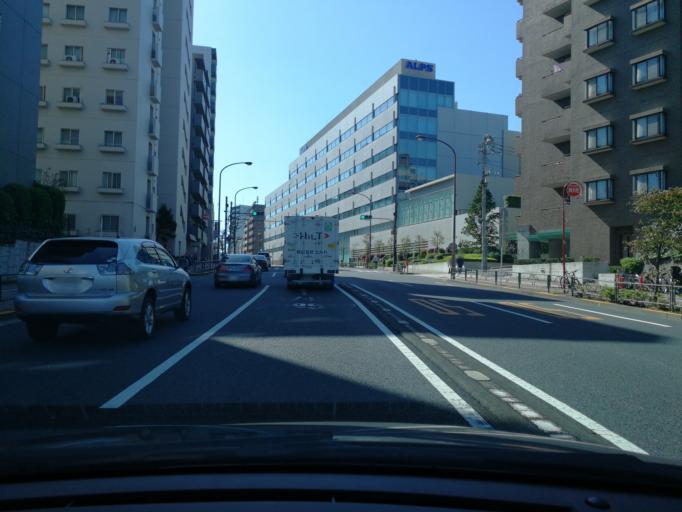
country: JP
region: Kanagawa
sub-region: Kawasaki-shi
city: Kawasaki
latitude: 35.5953
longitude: 139.6818
